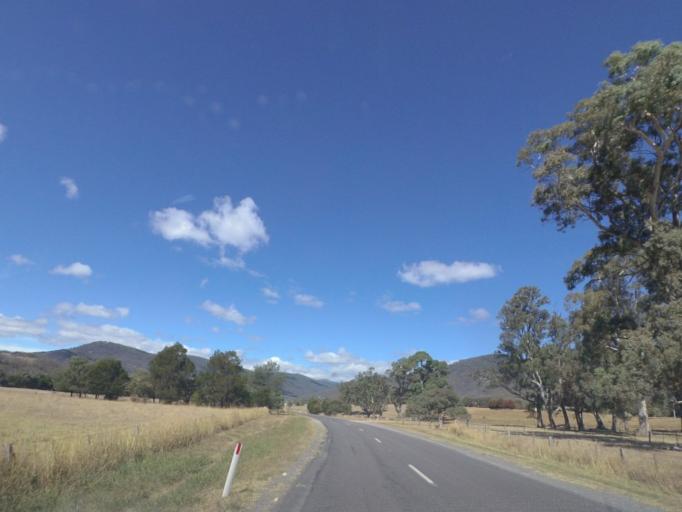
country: AU
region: Victoria
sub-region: Murrindindi
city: Alexandra
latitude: -37.2885
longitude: 145.8082
